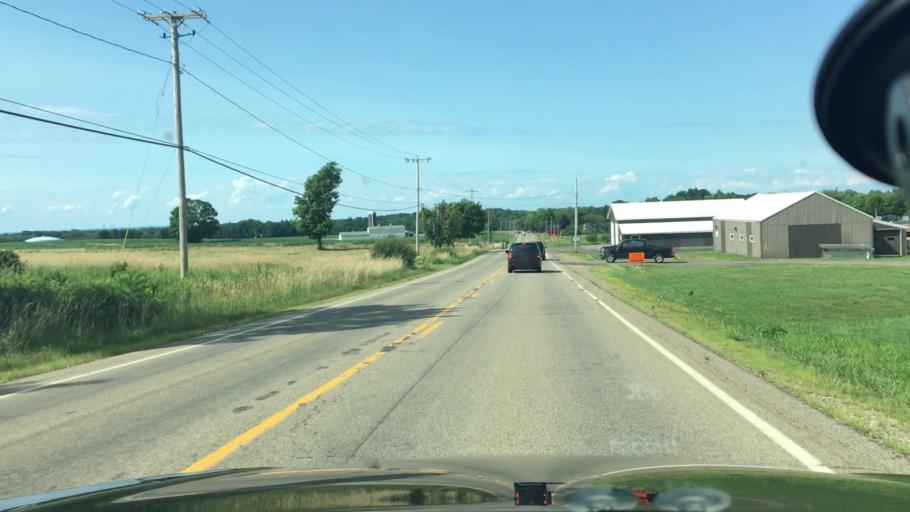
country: US
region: New York
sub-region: Chautauqua County
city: Fredonia
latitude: 42.4141
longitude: -79.3128
